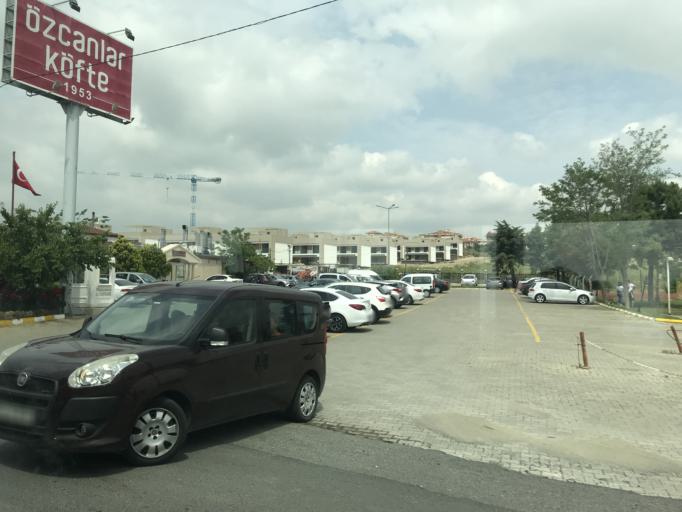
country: TR
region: Tekirdag
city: Tekirdag
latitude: 40.9896
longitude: 27.6034
